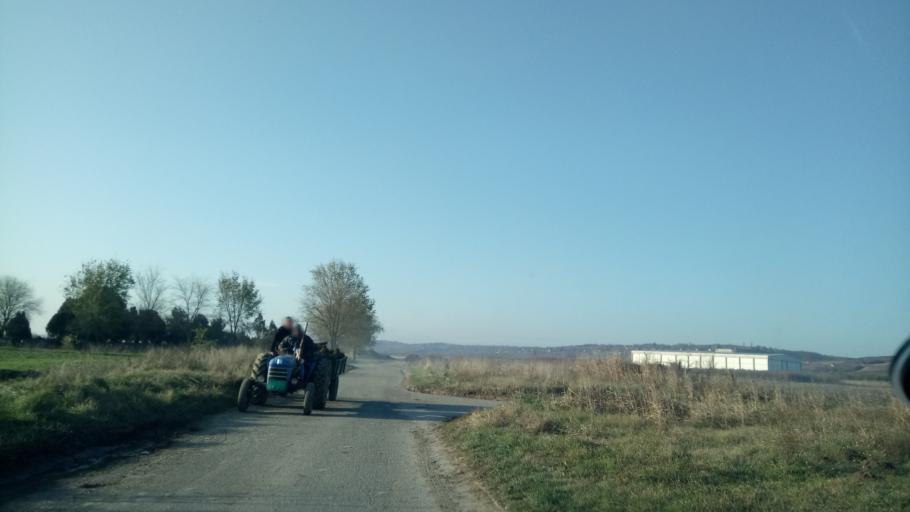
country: RS
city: Novi Slankamen
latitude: 45.1331
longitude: 20.2322
